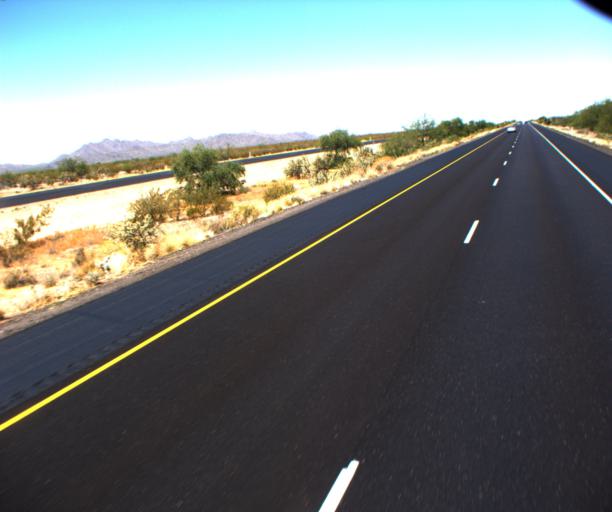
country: US
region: Arizona
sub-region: Yavapai County
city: Congress
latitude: 34.0677
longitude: -112.8705
